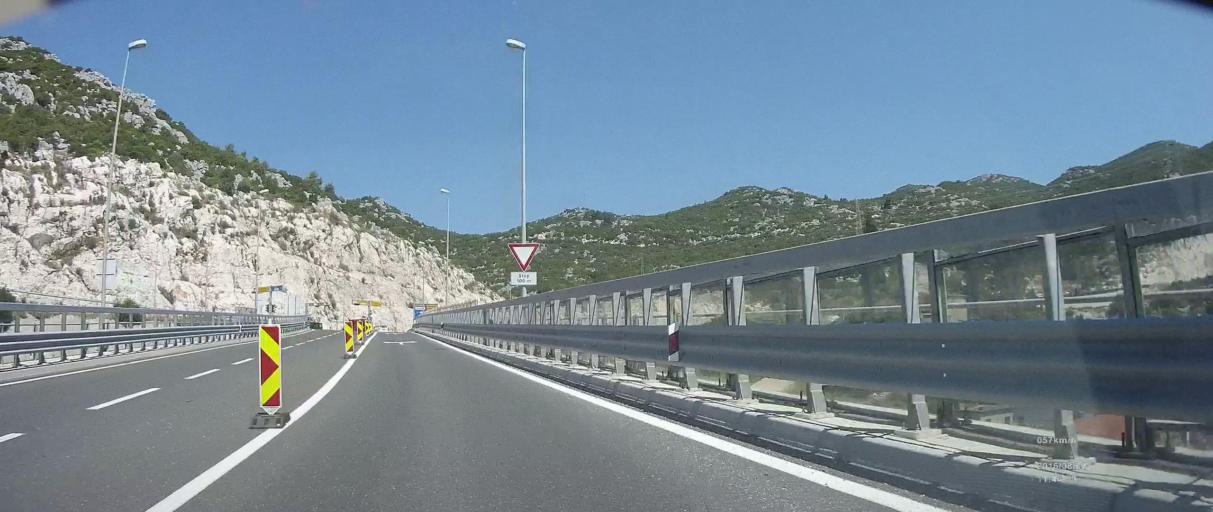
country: HR
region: Dubrovacko-Neretvanska
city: Komin
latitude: 43.0521
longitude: 17.4620
